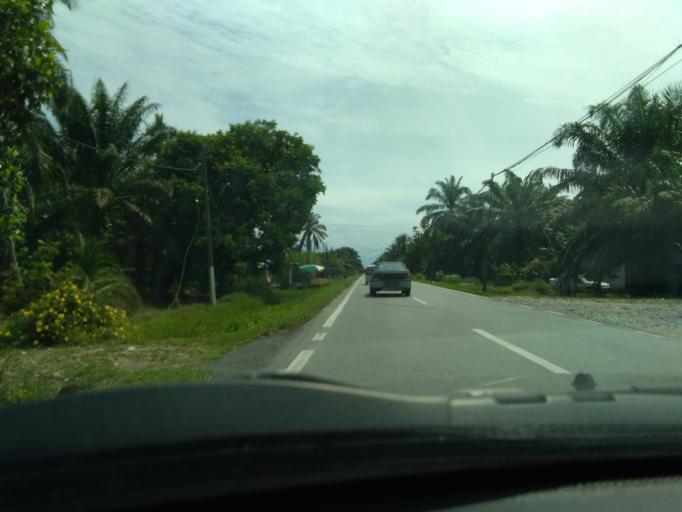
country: MY
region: Perak
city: Bagan Serai
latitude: 5.0370
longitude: 100.5688
